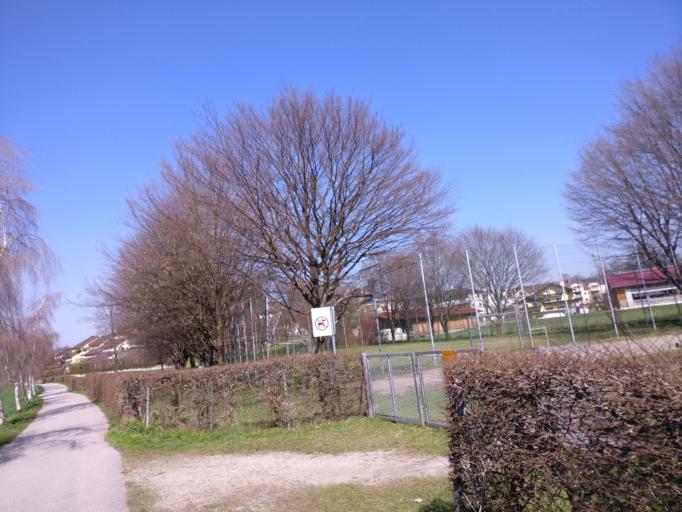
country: AT
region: Salzburg
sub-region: Salzburg Stadt
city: Salzburg
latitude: 47.7898
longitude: 13.0210
